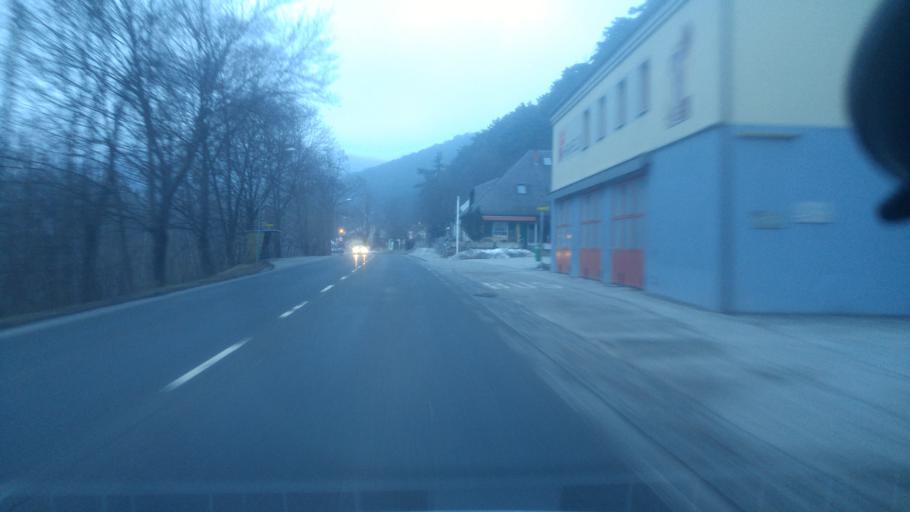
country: AT
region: Lower Austria
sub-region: Politischer Bezirk Baden
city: Weissenbach an der Triesting
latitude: 47.9781
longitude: 16.0688
